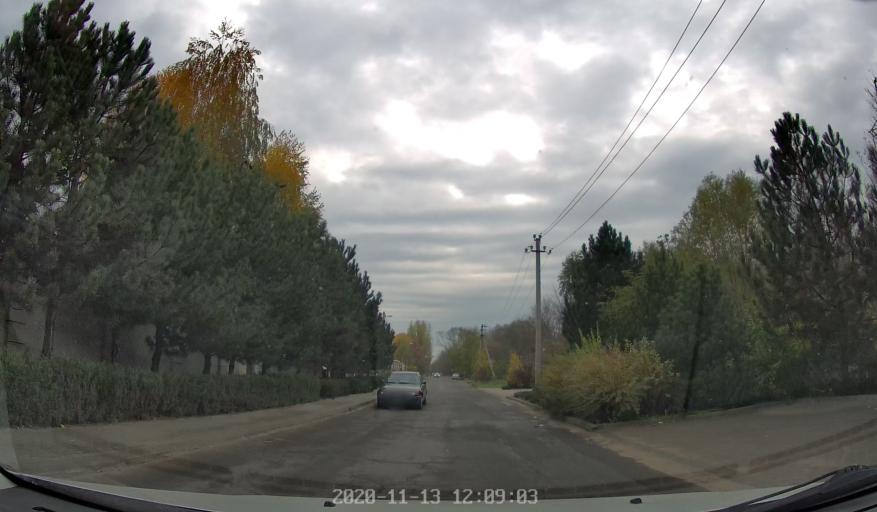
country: MD
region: Chisinau
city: Chisinau
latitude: 46.9612
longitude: 28.8352
